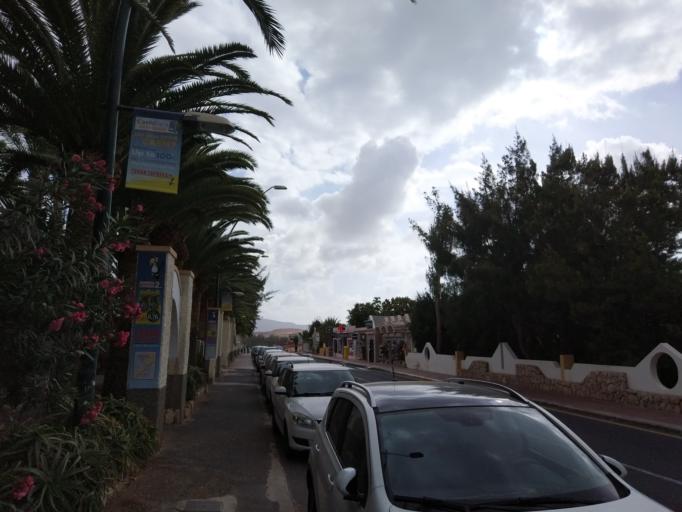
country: ES
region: Canary Islands
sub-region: Provincia de Las Palmas
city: Pajara
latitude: 28.1643
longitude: -14.2245
